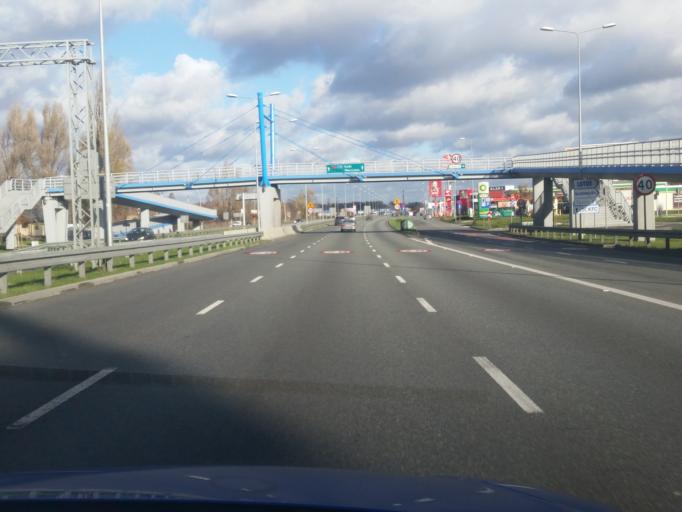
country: PL
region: Silesian Voivodeship
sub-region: Czestochowa
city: Czestochowa
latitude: 50.8187
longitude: 19.1390
